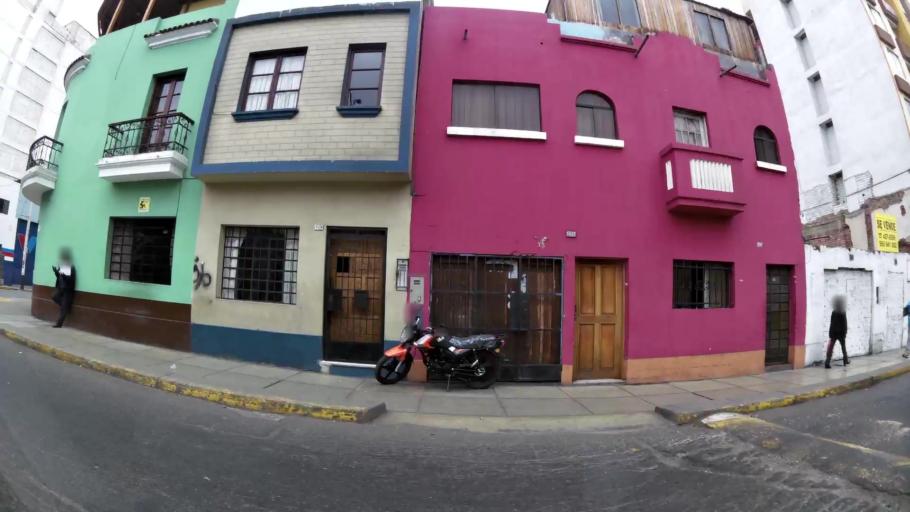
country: PE
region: Lima
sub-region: Lima
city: San Isidro
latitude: -12.0852
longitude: -77.0441
